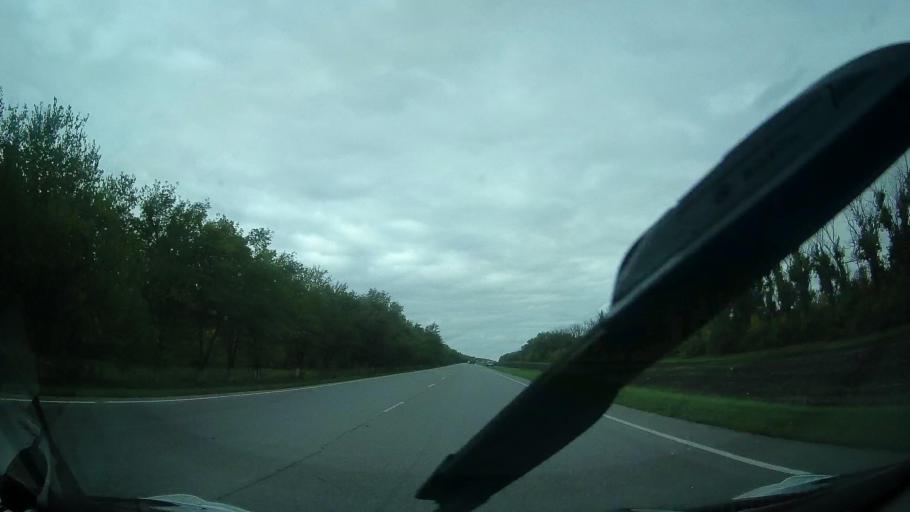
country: RU
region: Rostov
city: Yegorlykskaya
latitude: 46.6128
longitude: 40.6054
